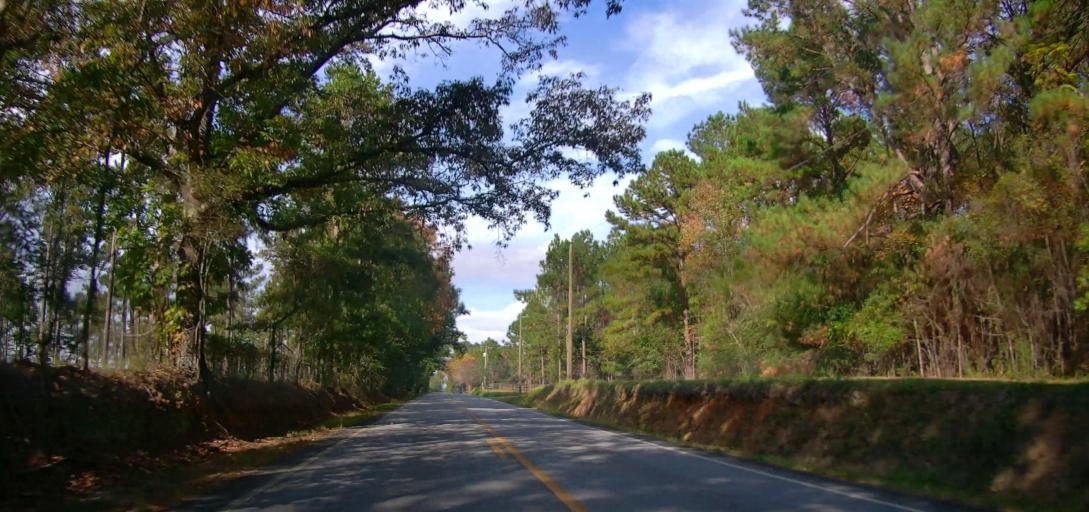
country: US
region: Georgia
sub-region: Thomas County
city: Thomasville
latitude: 30.8968
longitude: -84.0064
